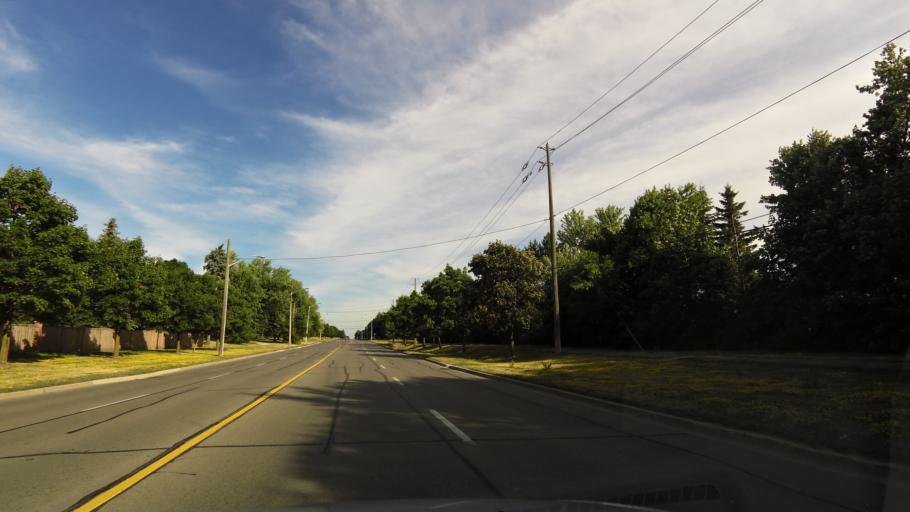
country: CA
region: Ontario
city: Brampton
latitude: 43.7369
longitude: -79.8054
